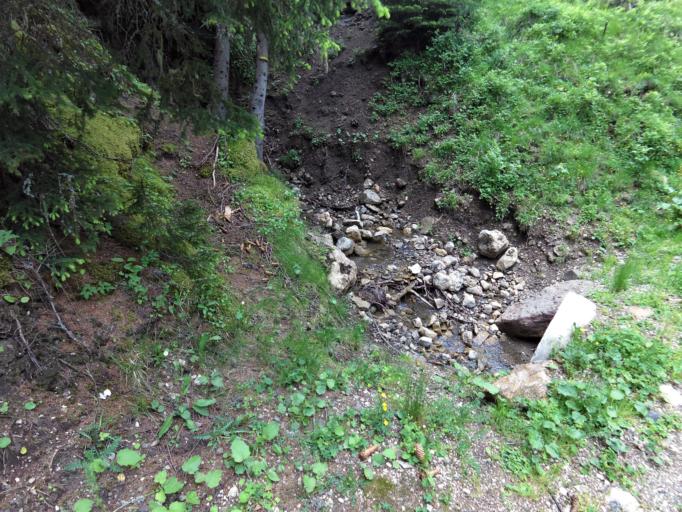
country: IT
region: Trentino-Alto Adige
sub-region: Bolzano
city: Ortisei
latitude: 46.5321
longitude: 11.6483
